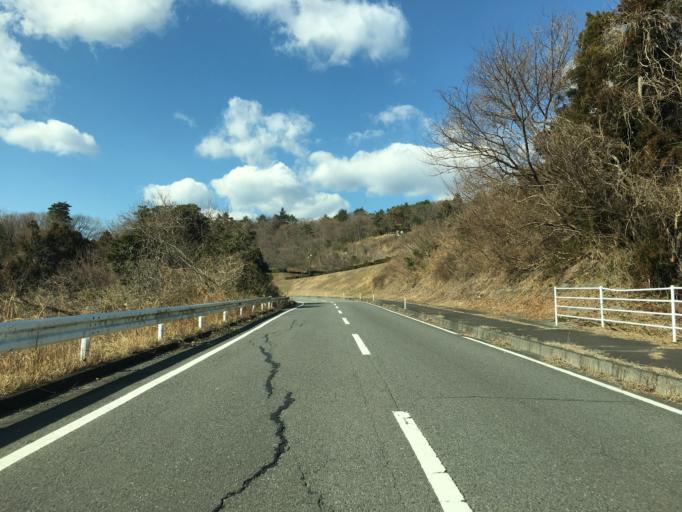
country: JP
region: Fukushima
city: Iwaki
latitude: 37.1203
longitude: 140.9858
